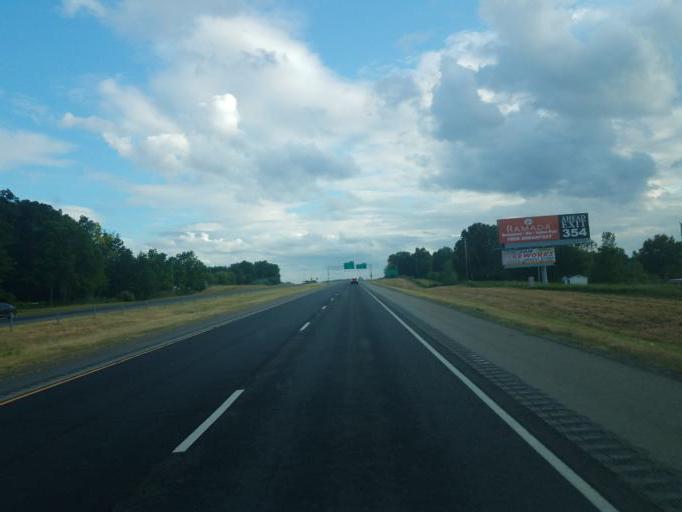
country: US
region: Indiana
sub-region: Steuben County
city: Fremont
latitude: 41.7563
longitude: -84.9916
